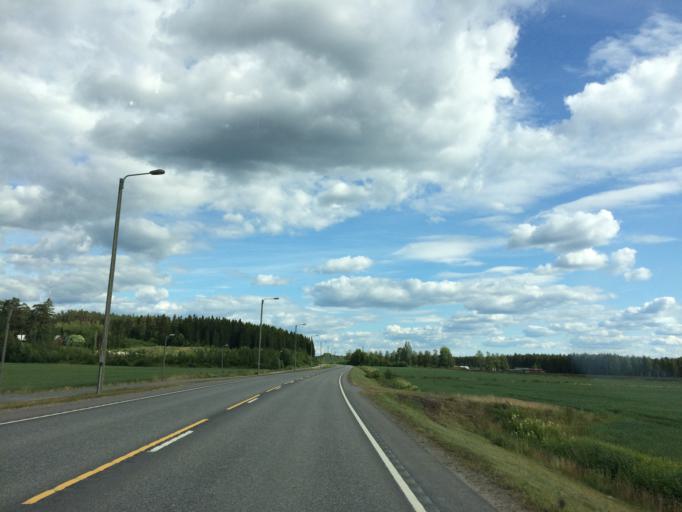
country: FI
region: Haeme
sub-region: Haemeenlinna
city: Turenki
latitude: 60.9530
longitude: 24.6049
